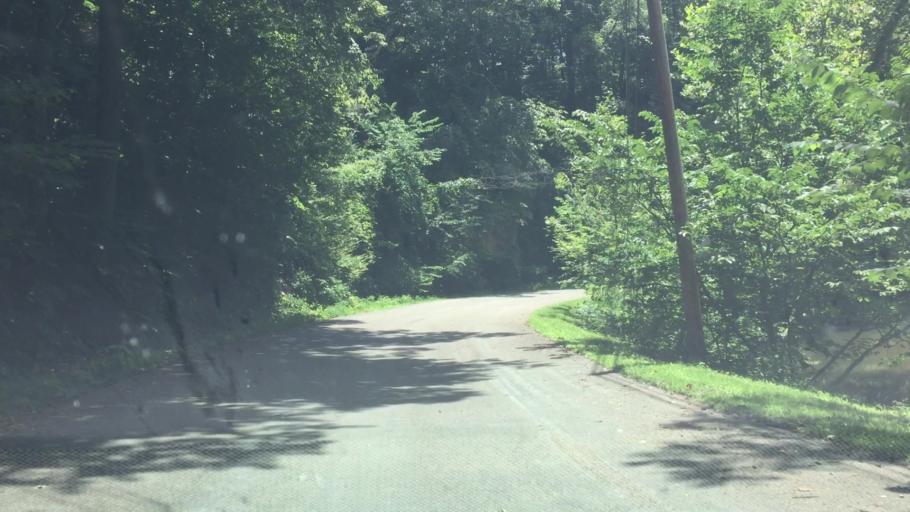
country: US
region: Virginia
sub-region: Pulaski County
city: Pulaski
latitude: 36.9525
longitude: -80.9018
